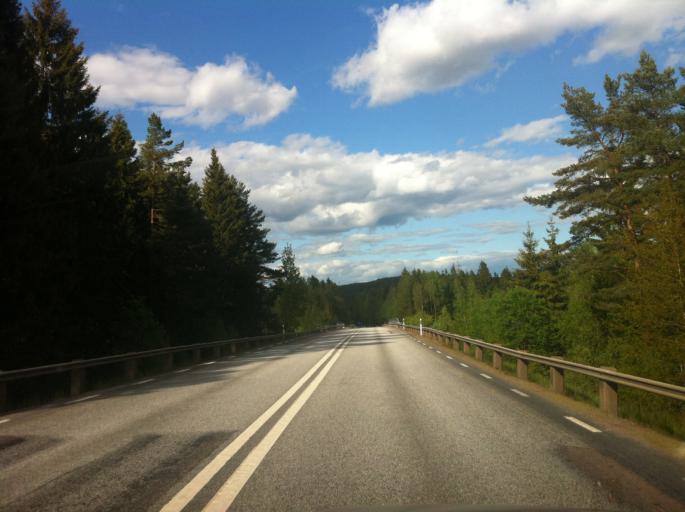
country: SE
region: Vaermland
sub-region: Storfors Kommun
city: Storfors
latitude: 59.5006
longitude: 14.2549
